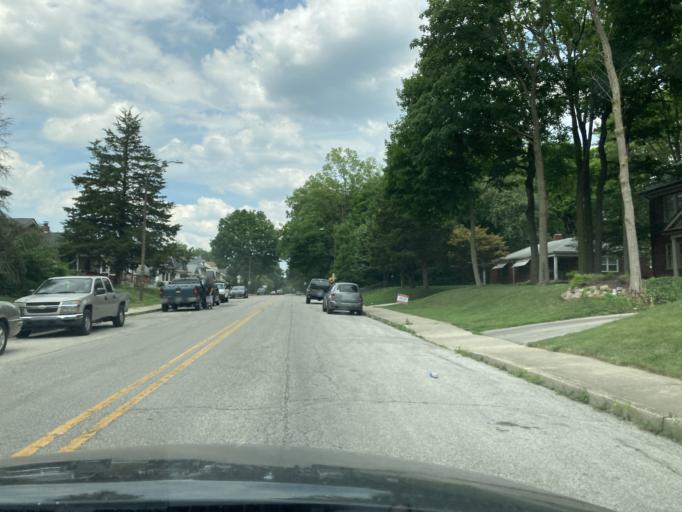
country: US
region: Indiana
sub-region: Marion County
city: Broad Ripple
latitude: 39.8305
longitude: -86.1616
